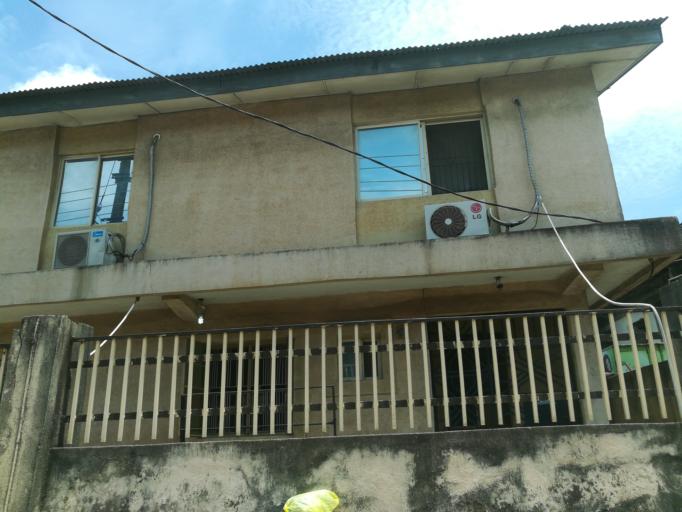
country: NG
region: Lagos
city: Ebute Ikorodu
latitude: 6.6015
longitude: 3.4936
